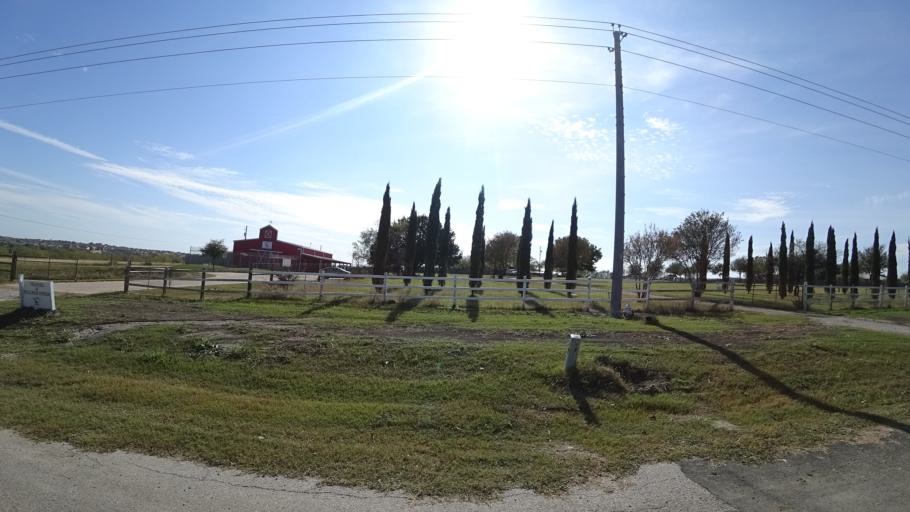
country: US
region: Texas
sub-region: Travis County
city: Pflugerville
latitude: 30.4024
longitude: -97.6216
